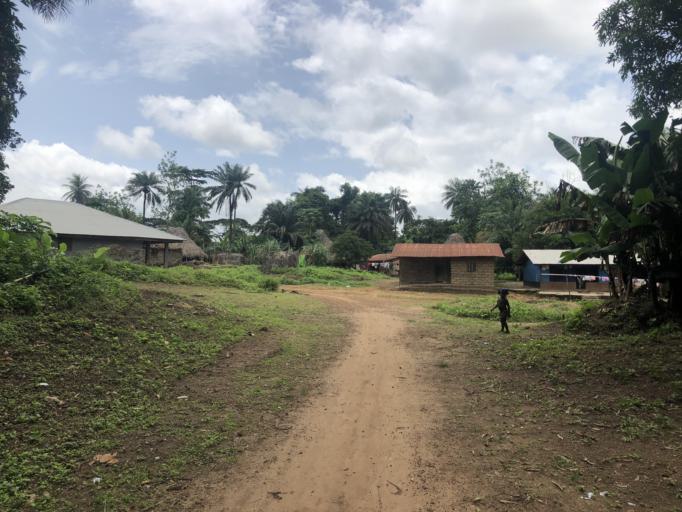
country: SL
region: Northern Province
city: Bumbuna
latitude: 9.0096
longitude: -11.8153
